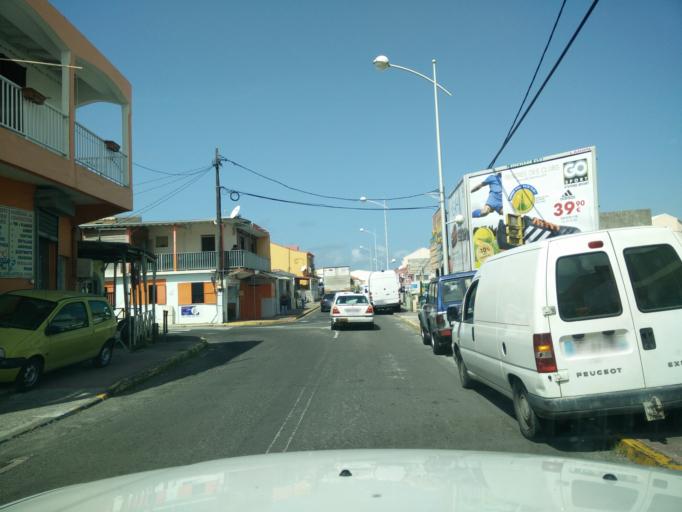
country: GP
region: Guadeloupe
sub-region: Guadeloupe
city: Le Gosier
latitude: 16.2063
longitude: -61.4866
